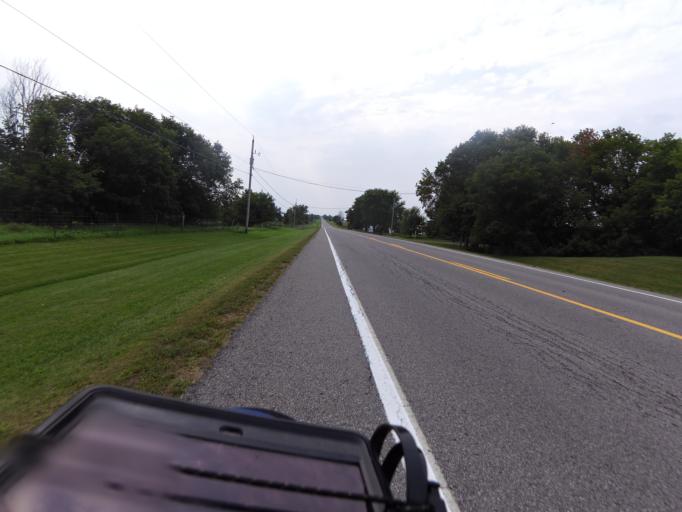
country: CA
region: Ontario
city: Casselman
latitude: 45.1685
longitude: -75.3087
